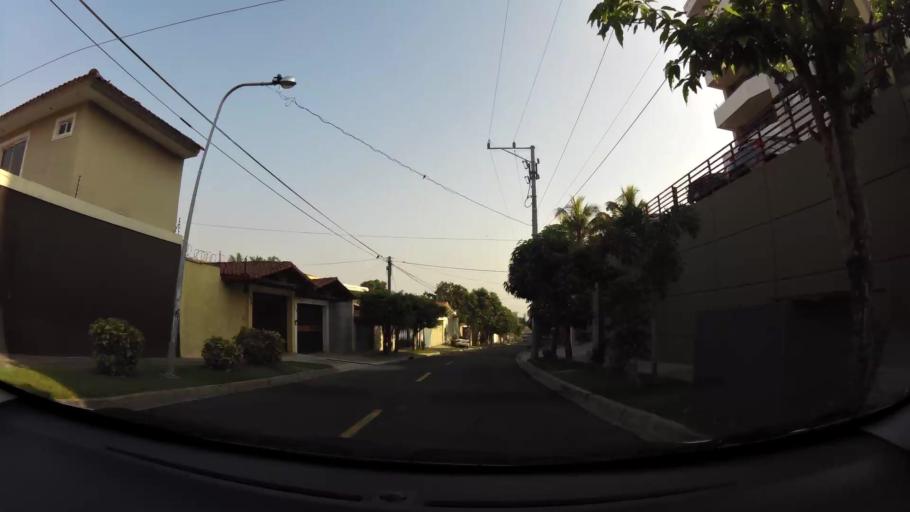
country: SV
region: La Libertad
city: Antiguo Cuscatlan
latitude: 13.6785
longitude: -89.2224
